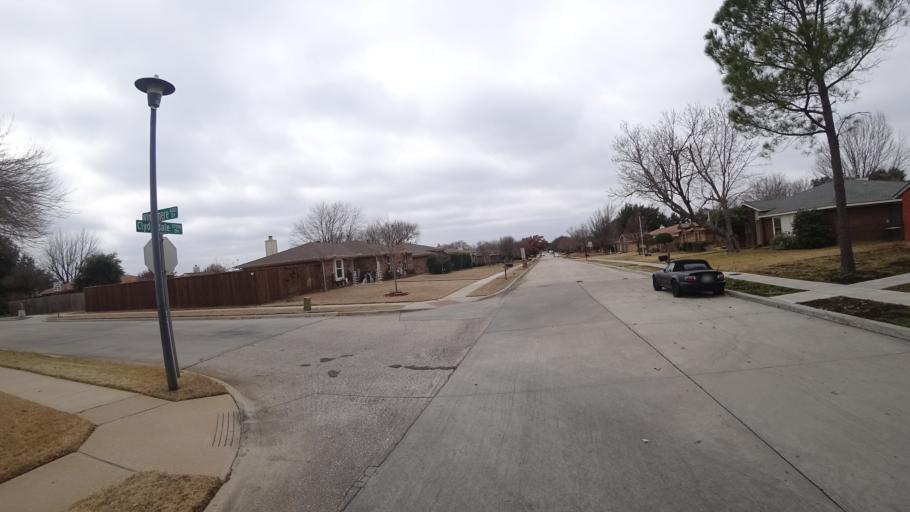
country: US
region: Texas
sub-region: Denton County
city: Lewisville
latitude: 33.0454
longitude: -97.0400
